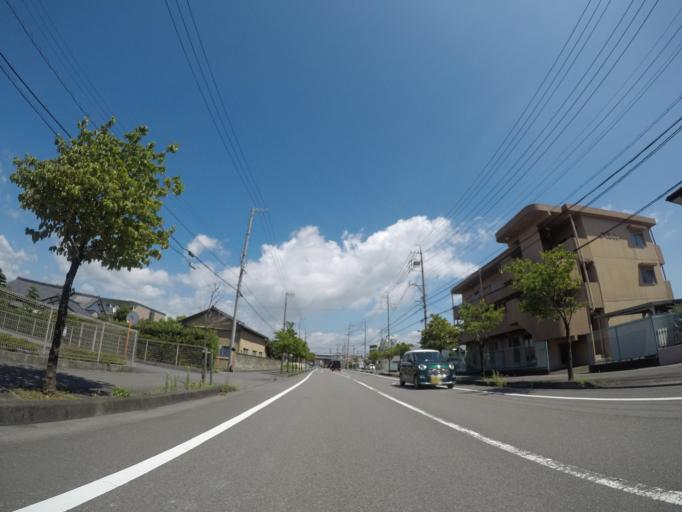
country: JP
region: Shizuoka
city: Fujieda
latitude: 34.8575
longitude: 138.2884
